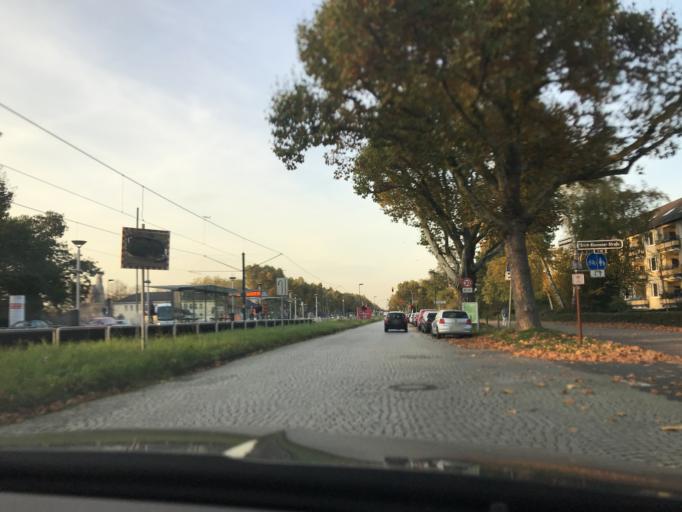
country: DE
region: North Rhine-Westphalia
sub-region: Regierungsbezirk Dusseldorf
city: Dusseldorf
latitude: 51.2559
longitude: 6.7559
